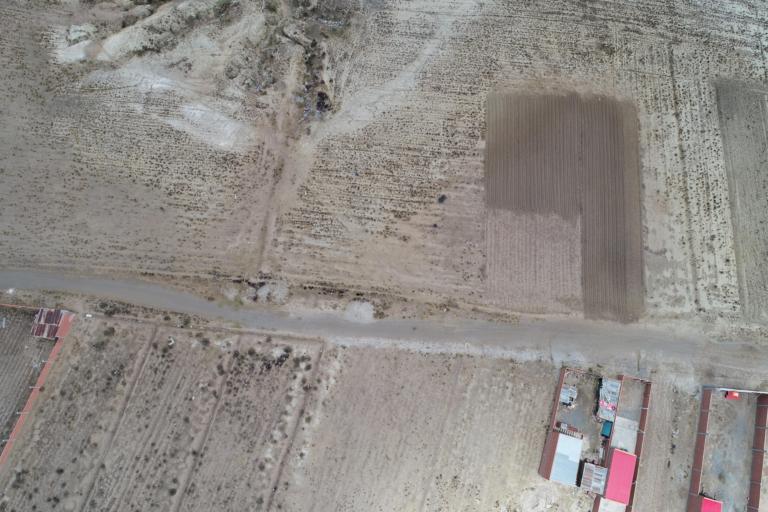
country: BO
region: La Paz
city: Achacachi
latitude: -16.0447
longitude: -68.6942
